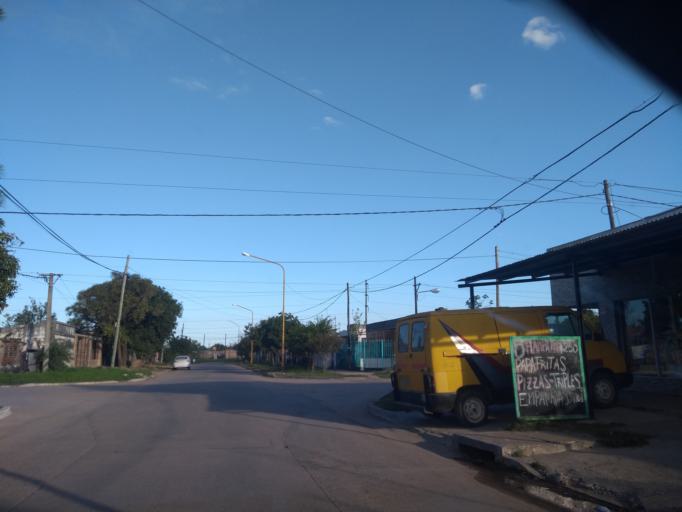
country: AR
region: Chaco
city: Barranqueras
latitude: -27.4869
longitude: -58.9427
